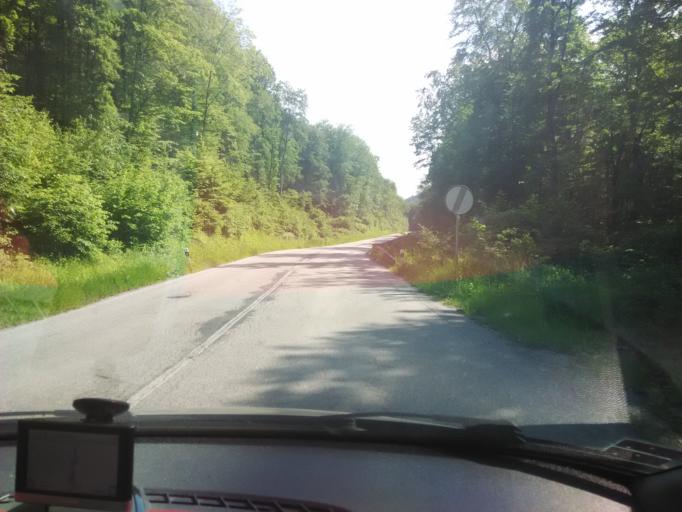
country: SK
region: Banskobystricky
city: Revuca
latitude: 48.6372
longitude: 20.2900
